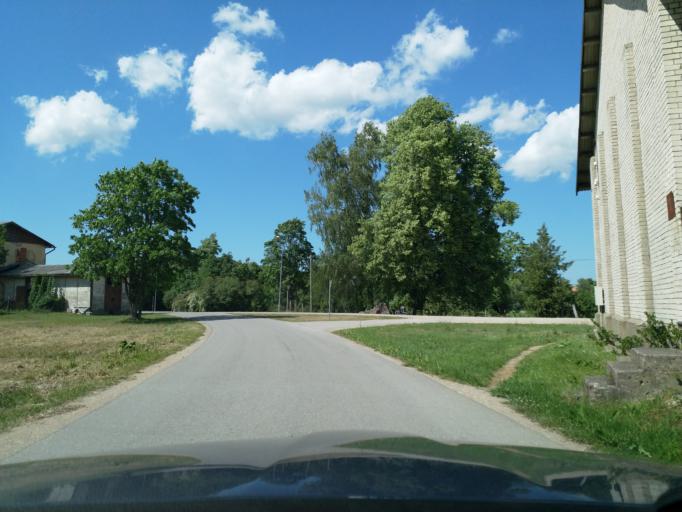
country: LV
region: Alsunga
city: Alsunga
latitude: 56.9765
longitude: 21.5662
